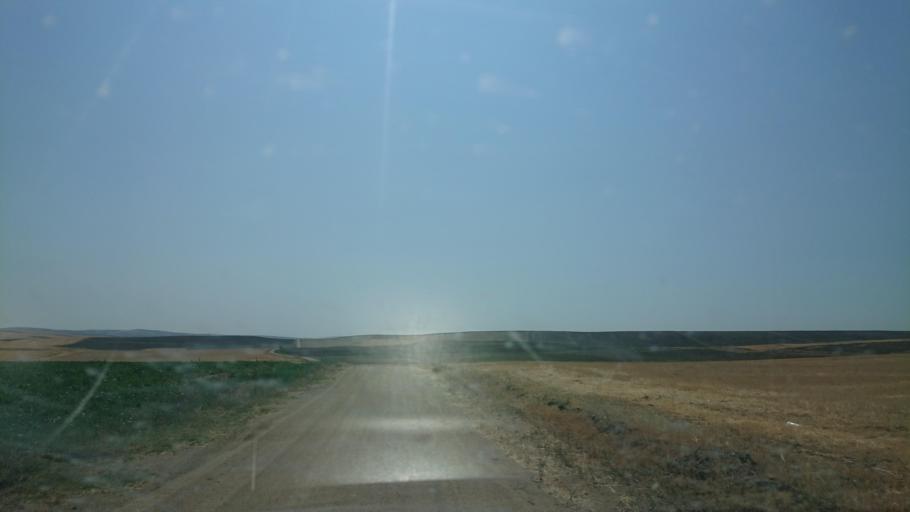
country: TR
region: Aksaray
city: Sariyahsi
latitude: 38.9564
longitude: 33.9149
